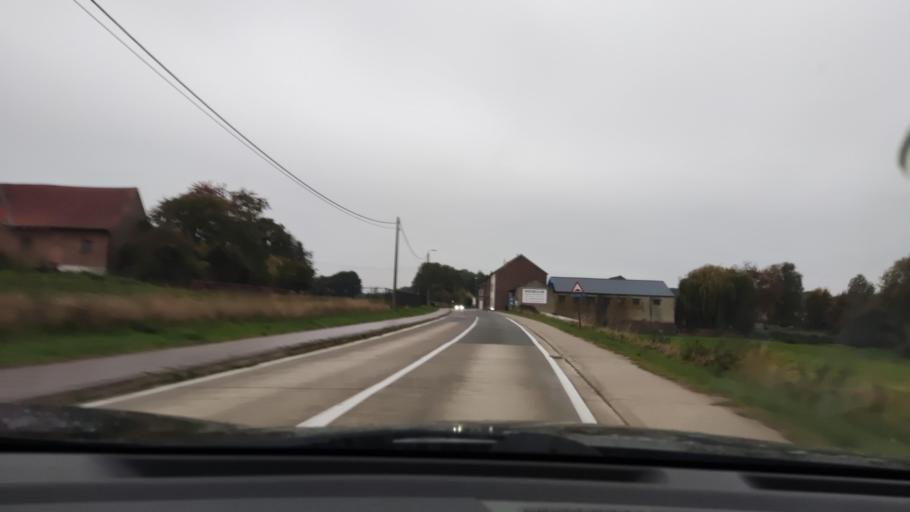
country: BE
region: Flanders
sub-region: Provincie Vlaams-Brabant
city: Hoegaarden
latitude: 50.7863
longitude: 4.8465
